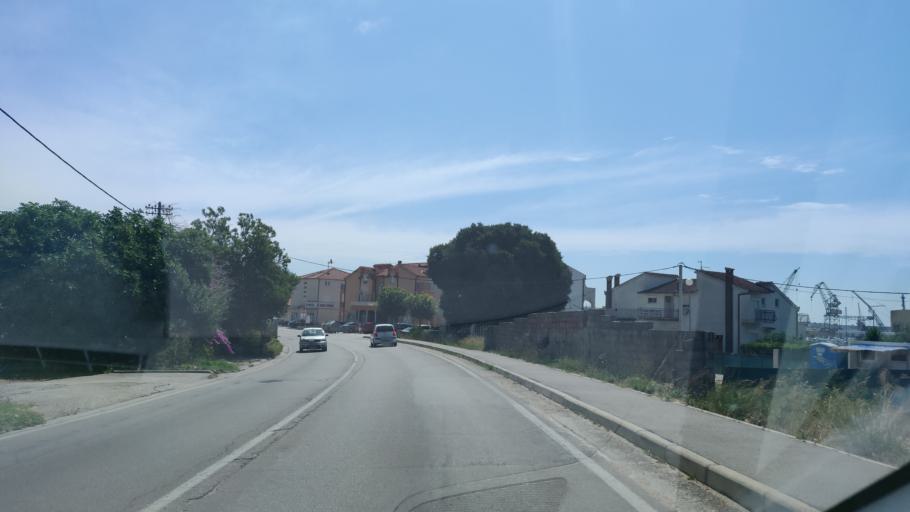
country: HR
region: Splitsko-Dalmatinska
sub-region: Grad Trogir
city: Trogir
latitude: 43.5177
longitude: 16.2378
